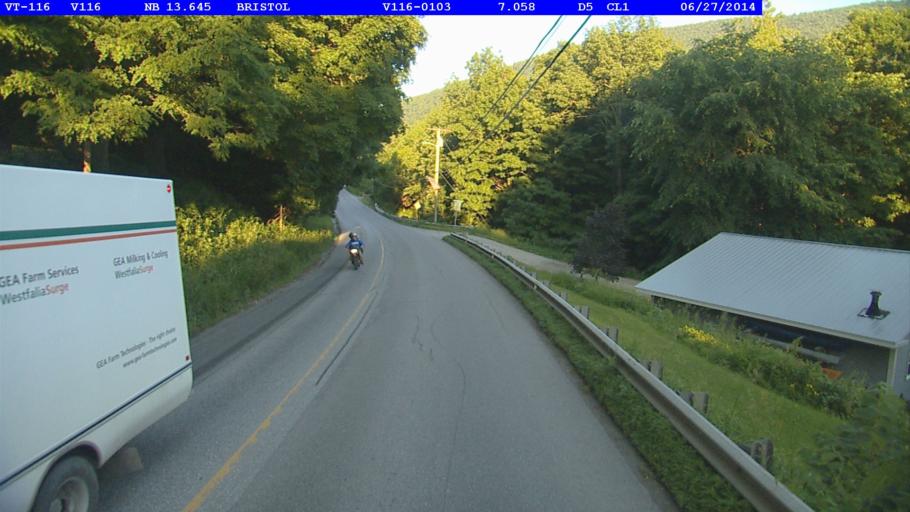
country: US
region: Vermont
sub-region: Addison County
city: Bristol
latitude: 44.1303
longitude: -73.0712
